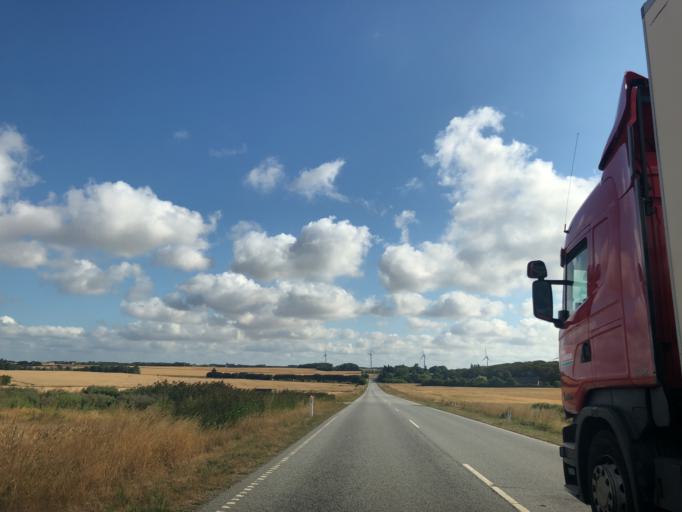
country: DK
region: Central Jutland
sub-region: Skive Kommune
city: Skive
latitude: 56.6635
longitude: 8.9448
